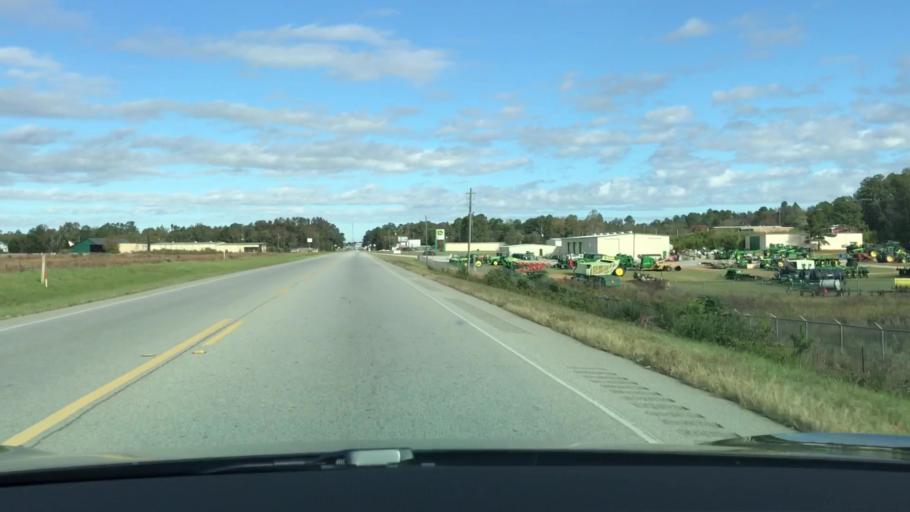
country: US
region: Georgia
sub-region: Jefferson County
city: Louisville
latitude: 32.9907
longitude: -82.3934
